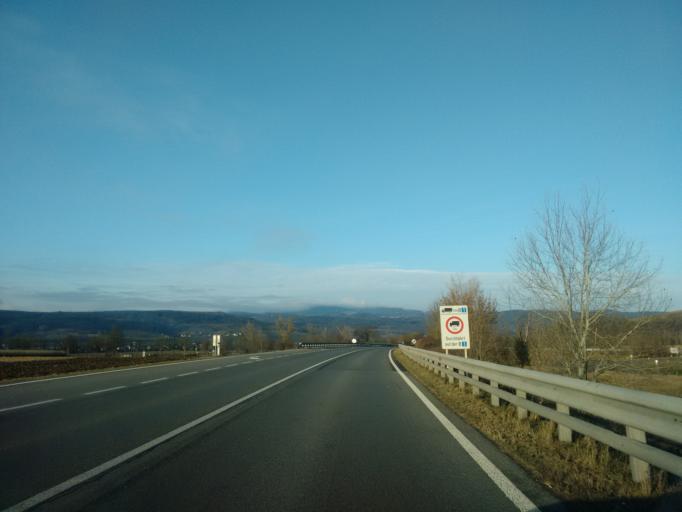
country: AT
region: Lower Austria
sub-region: Politischer Bezirk Melk
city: Emmersdorf an der Donau
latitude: 48.2314
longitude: 15.3479
